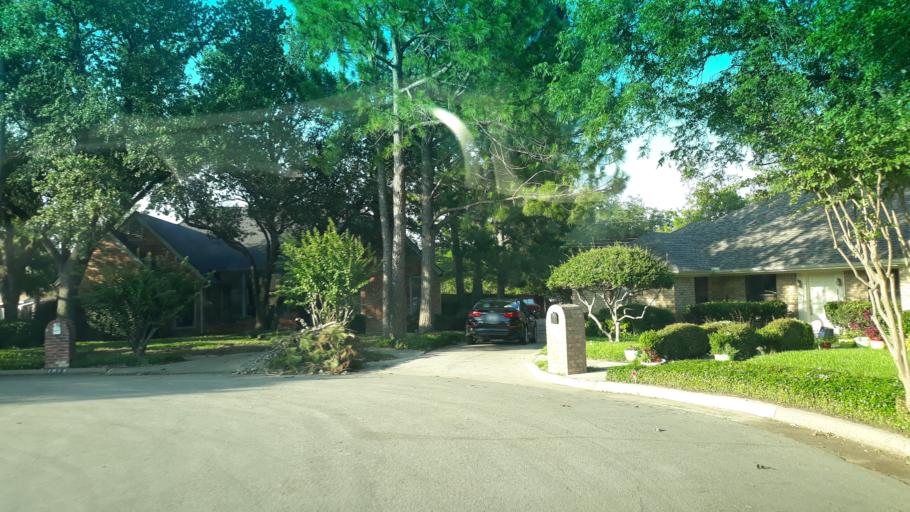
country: US
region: Texas
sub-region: Dallas County
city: Irving
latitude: 32.8607
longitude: -97.0000
